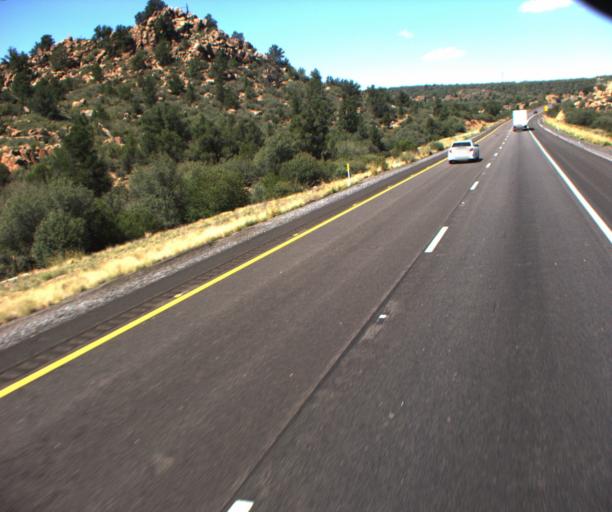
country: US
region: Arizona
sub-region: Mohave County
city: Peach Springs
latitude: 35.1908
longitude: -113.3910
